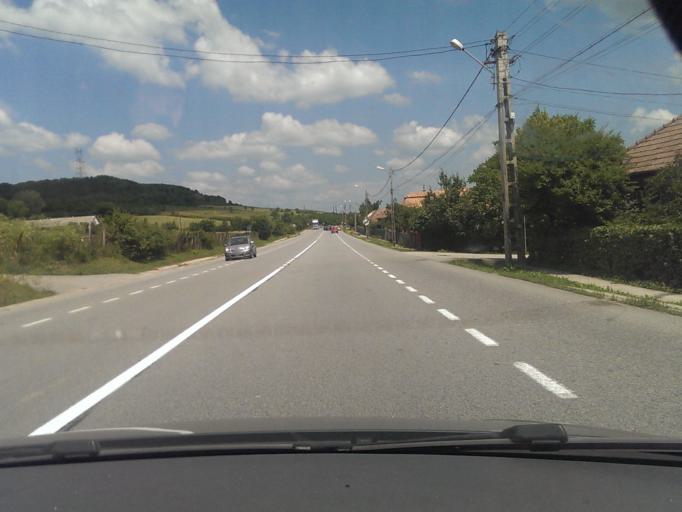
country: RO
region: Cluj
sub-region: Comuna Bontida
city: Rascruci
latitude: 46.9101
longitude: 23.7756
